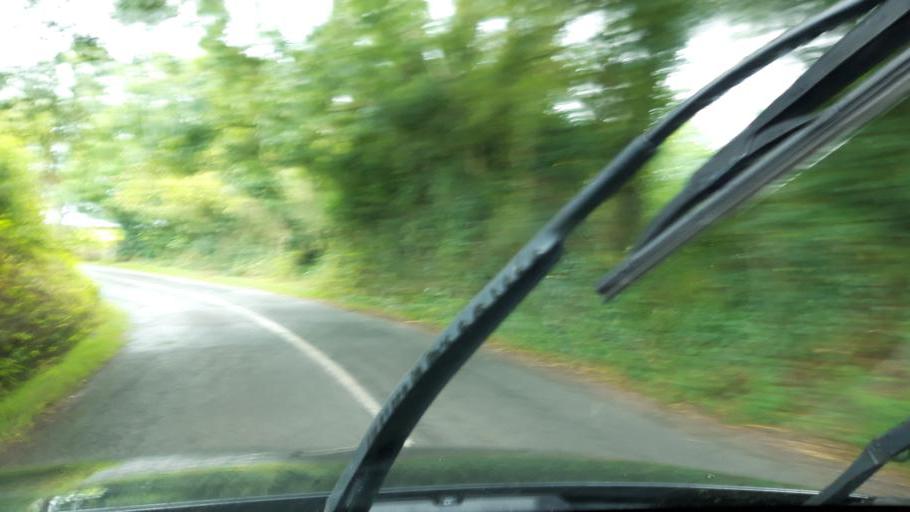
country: IE
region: Munster
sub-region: County Cork
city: Fermoy
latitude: 52.1416
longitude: -8.0487
